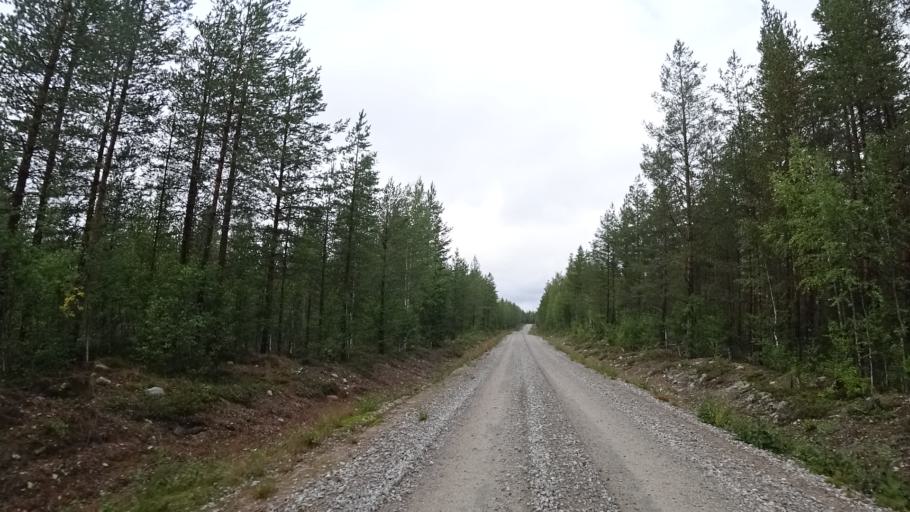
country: FI
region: North Karelia
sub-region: Pielisen Karjala
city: Lieksa
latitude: 63.4673
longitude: 30.2873
